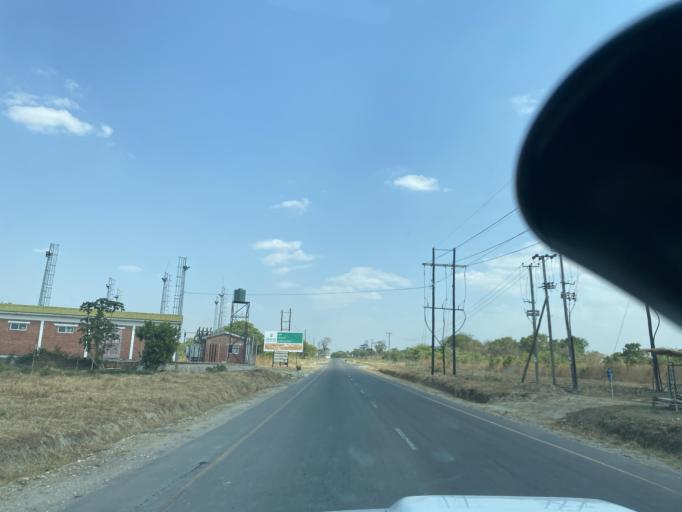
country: ZM
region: Lusaka
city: Lusaka
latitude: -15.3364
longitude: 28.0740
